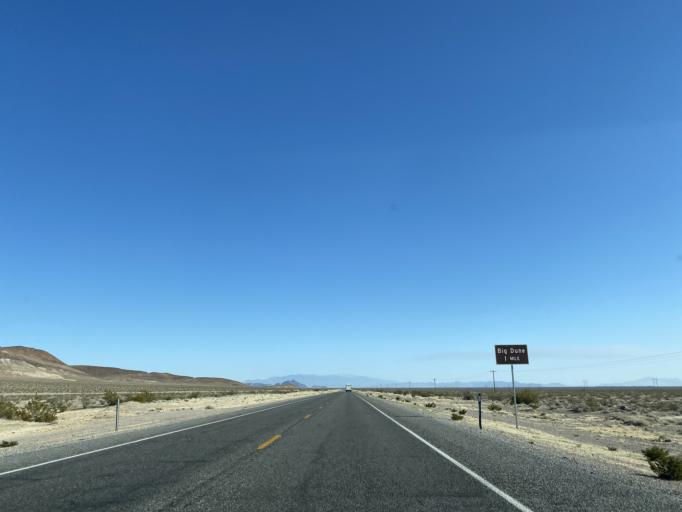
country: US
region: Nevada
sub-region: Nye County
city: Beatty
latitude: 36.6881
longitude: -116.5583
